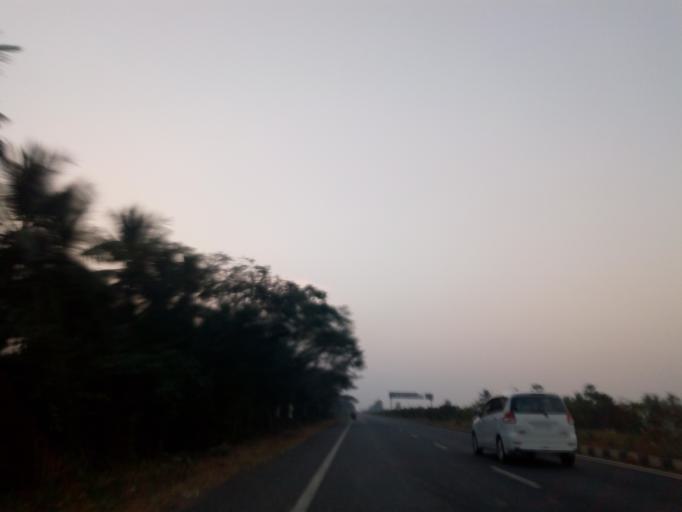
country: IN
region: Andhra Pradesh
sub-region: West Godavari
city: Tadepallegudem
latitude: 16.8243
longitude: 81.4532
